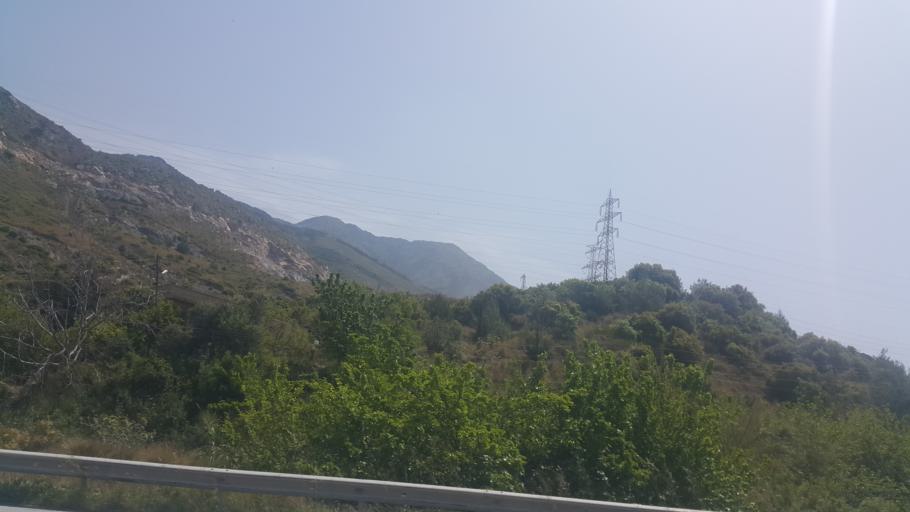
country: TR
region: Hatay
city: Iskenderun
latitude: 36.5754
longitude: 36.2043
